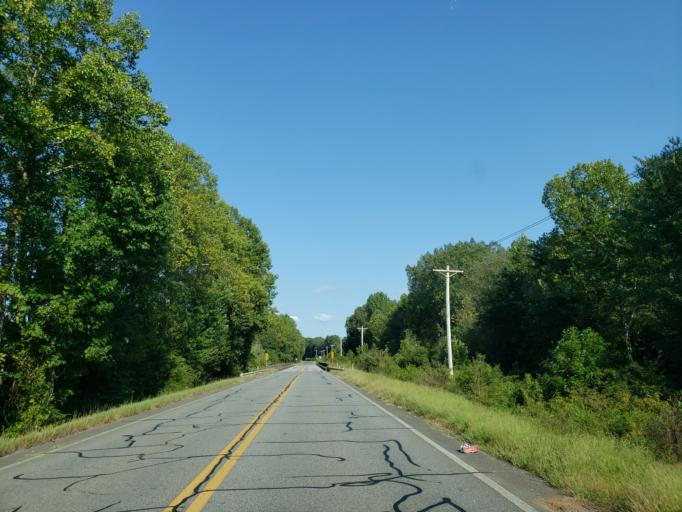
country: US
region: Georgia
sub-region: Whitfield County
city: Varnell
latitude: 34.9214
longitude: -84.8389
